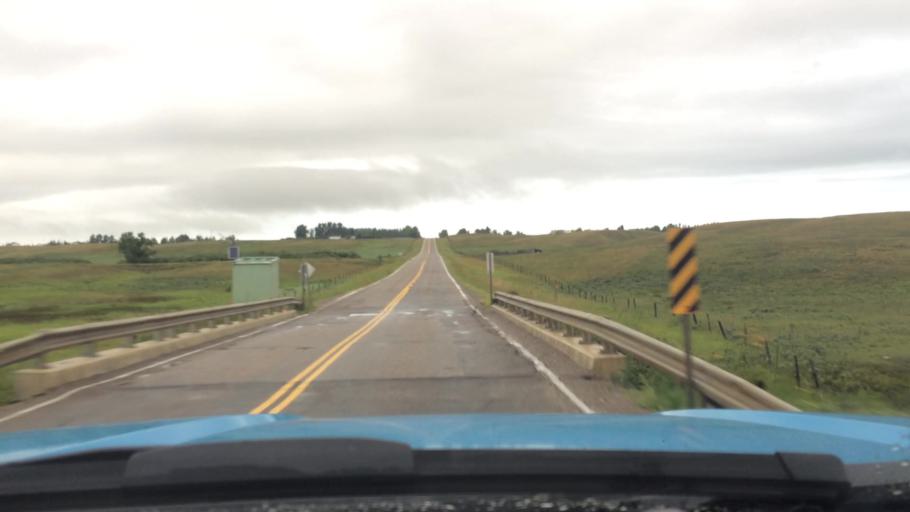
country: CA
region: Alberta
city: Calgary
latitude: 51.1897
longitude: -114.1412
